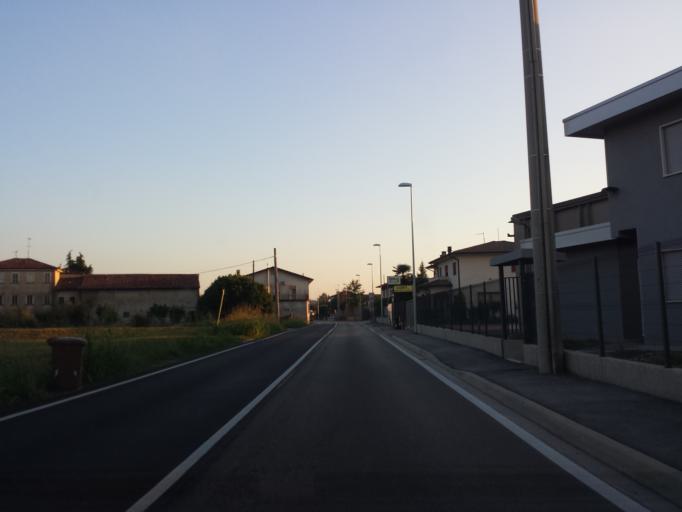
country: IT
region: Veneto
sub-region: Provincia di Vicenza
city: Vicenza
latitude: 45.5721
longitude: 11.5595
